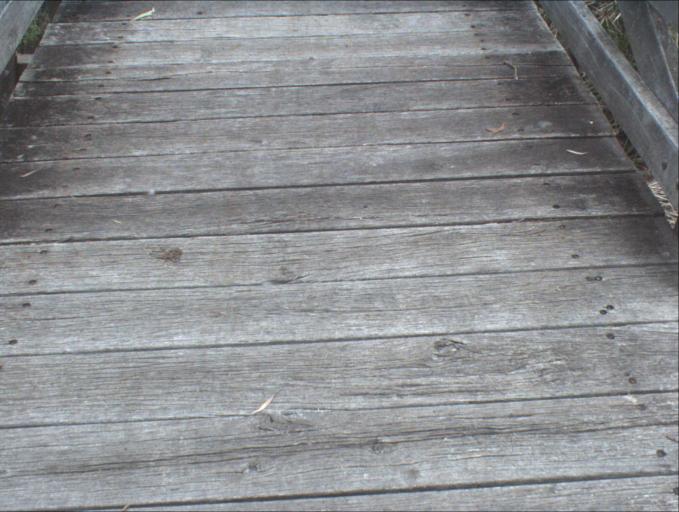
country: AU
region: Queensland
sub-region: Logan
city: Park Ridge South
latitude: -27.6901
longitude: 153.0265
